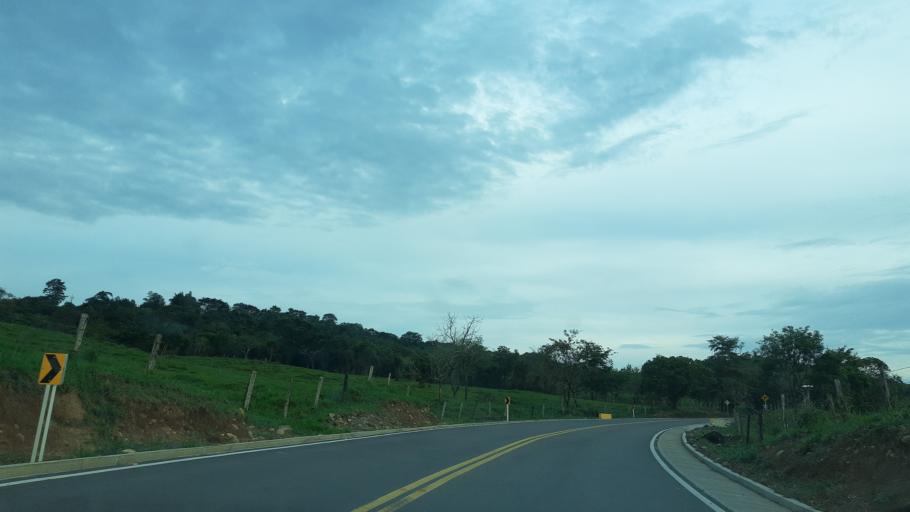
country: CO
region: Casanare
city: Sabanalarga
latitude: 4.8114
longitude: -73.0592
